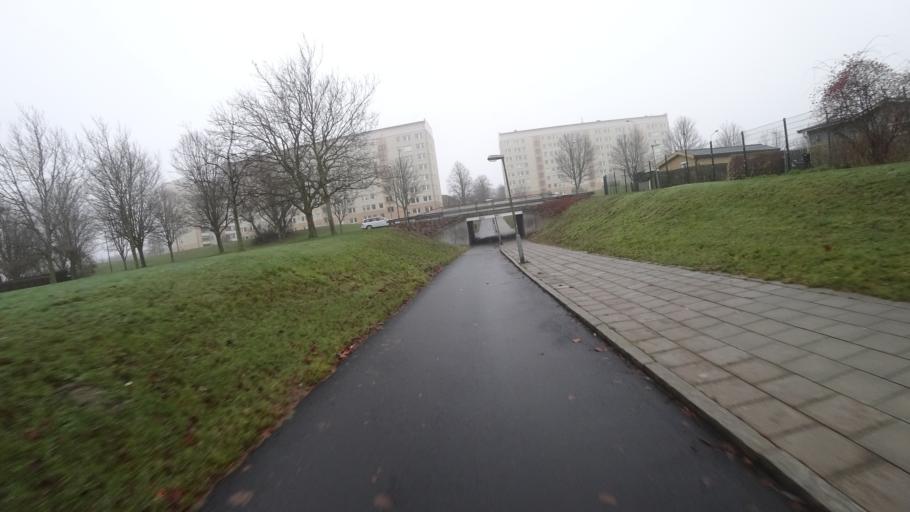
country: SE
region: Skane
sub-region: Malmo
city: Malmoe
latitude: 55.5763
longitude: 12.9873
